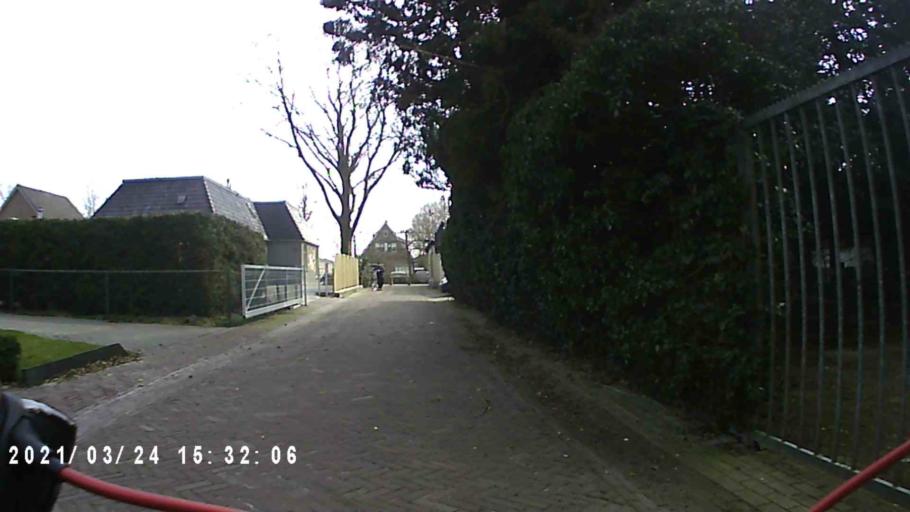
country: NL
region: Friesland
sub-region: Gemeente Heerenveen
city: Jubbega
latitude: 53.0052
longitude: 6.1235
